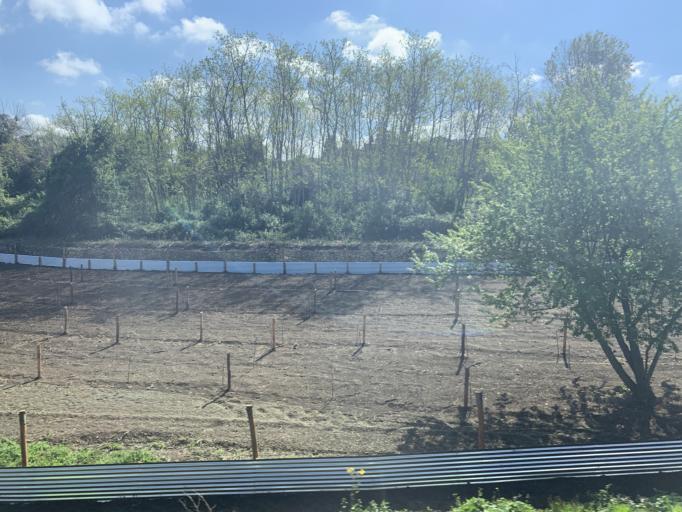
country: IT
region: Latium
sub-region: Citta metropolitana di Roma Capitale
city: Marino
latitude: 41.7731
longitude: 12.6463
